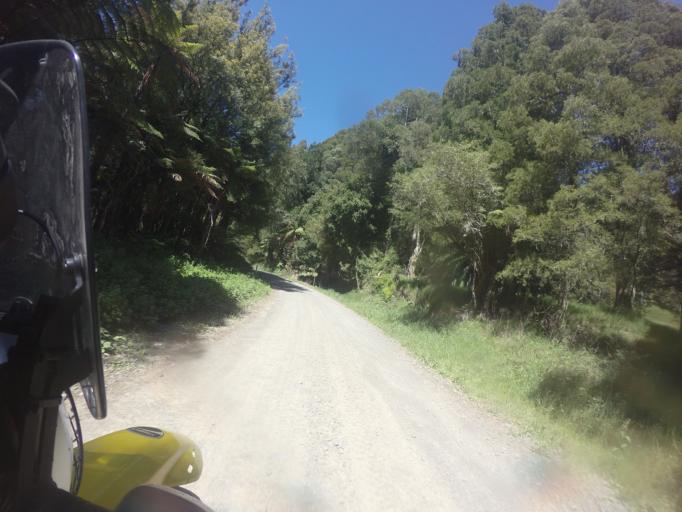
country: NZ
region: Bay of Plenty
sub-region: Opotiki District
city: Opotiki
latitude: -38.2899
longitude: 177.3422
